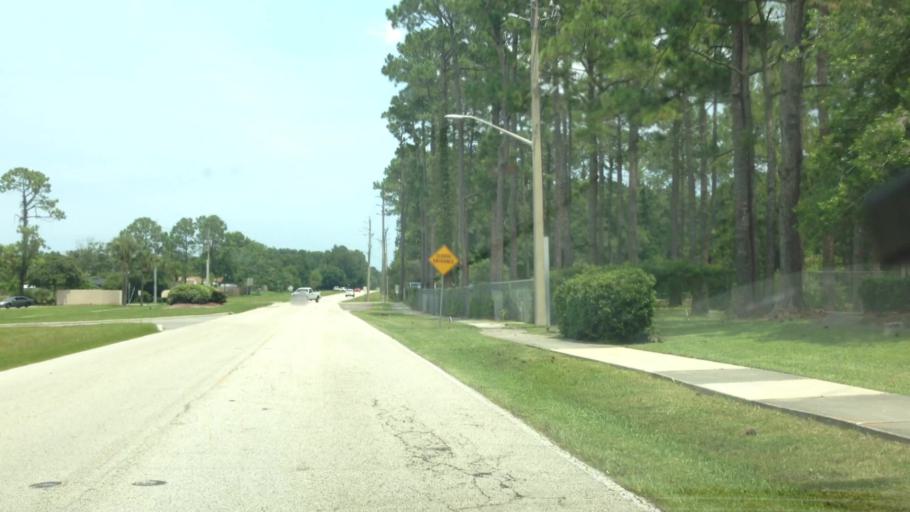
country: US
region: Florida
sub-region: Duval County
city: Neptune Beach
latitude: 30.3015
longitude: -81.5145
